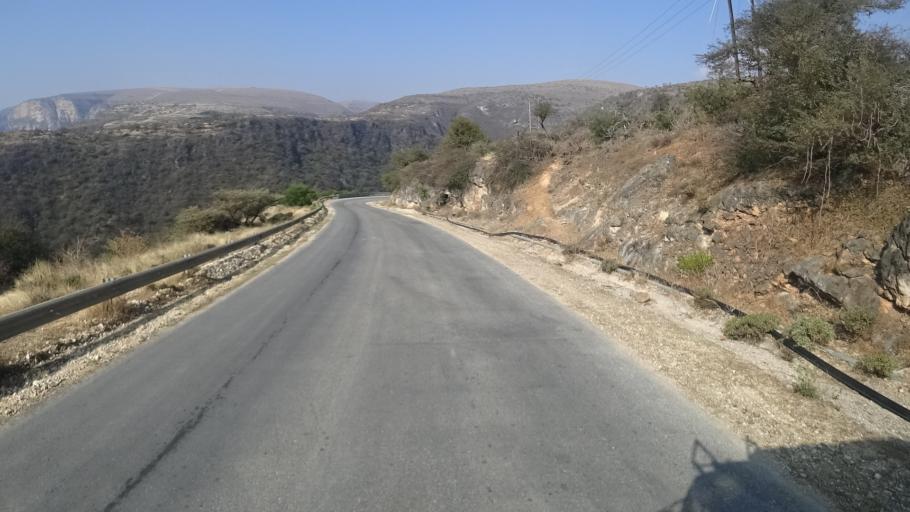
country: YE
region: Al Mahrah
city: Hawf
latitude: 16.7094
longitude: 53.1457
